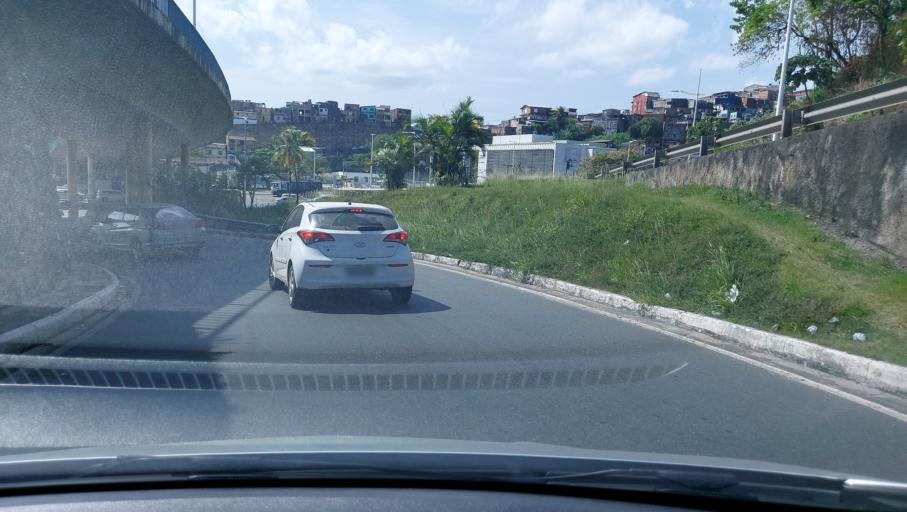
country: BR
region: Bahia
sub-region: Salvador
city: Salvador
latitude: -12.9522
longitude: -38.4742
